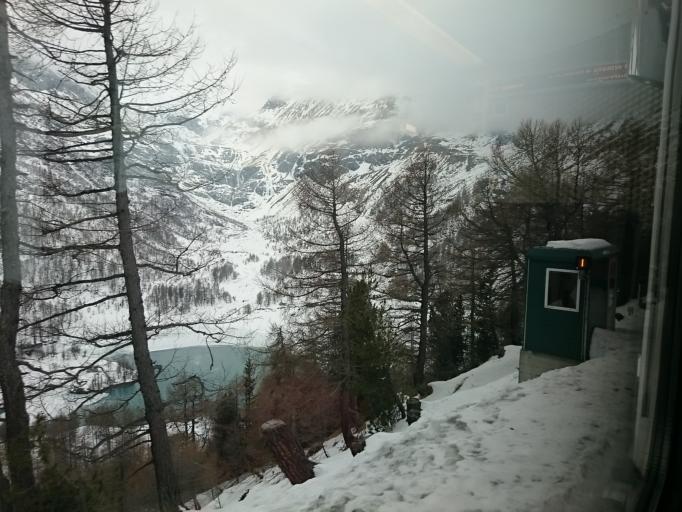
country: CH
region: Grisons
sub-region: Bernina District
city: Poschiavo
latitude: 46.3735
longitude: 10.0316
